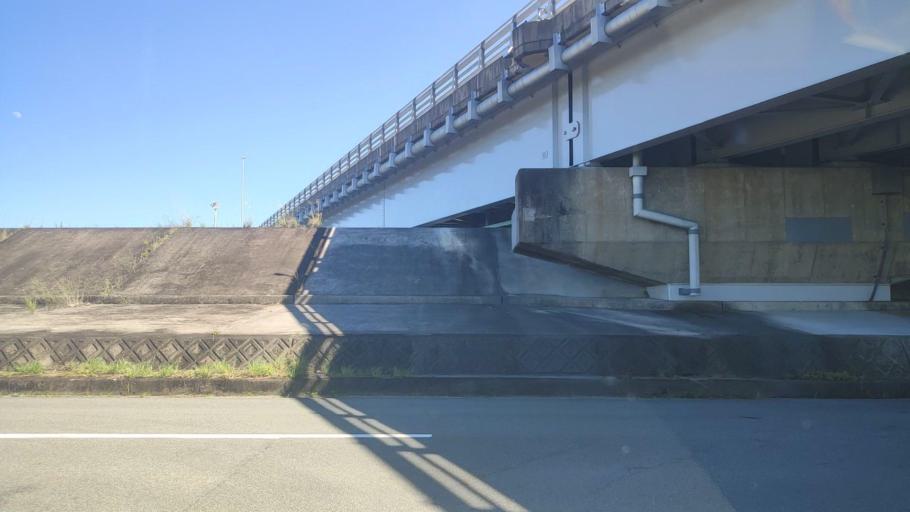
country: JP
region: Mie
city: Ise
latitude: 34.5142
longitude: 136.6931
